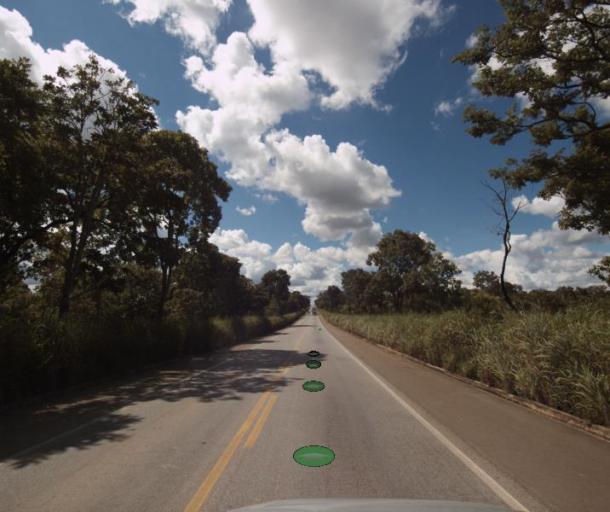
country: BR
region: Goias
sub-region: Porangatu
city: Porangatu
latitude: -13.6252
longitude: -49.0427
